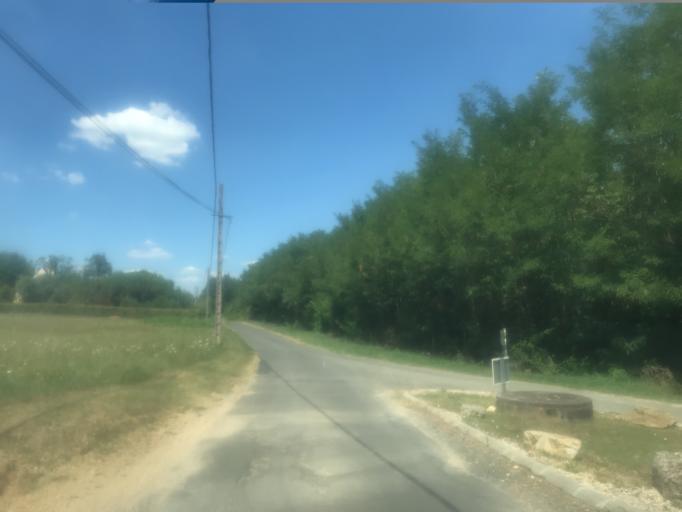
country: FR
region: Aquitaine
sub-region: Departement de la Dordogne
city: Cenac-et-Saint-Julien
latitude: 44.8290
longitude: 1.1926
